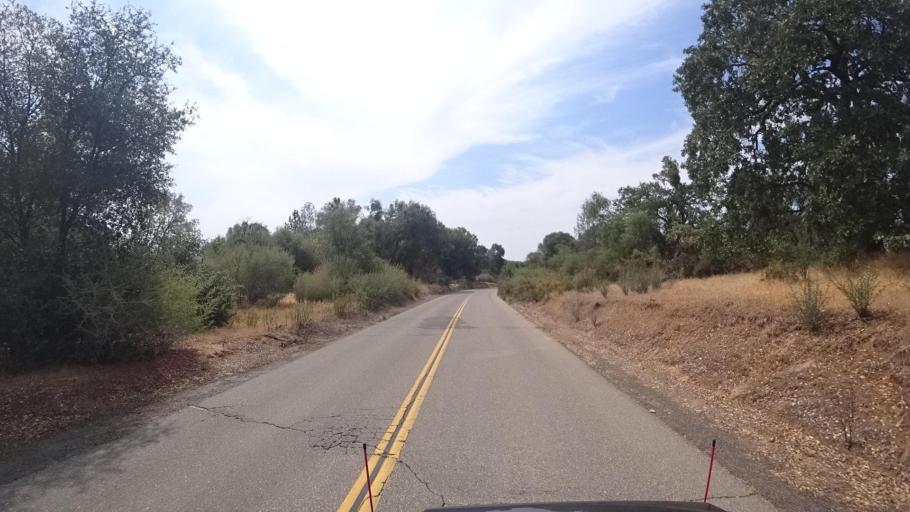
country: US
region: California
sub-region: Mariposa County
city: Midpines
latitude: 37.5007
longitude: -119.8901
